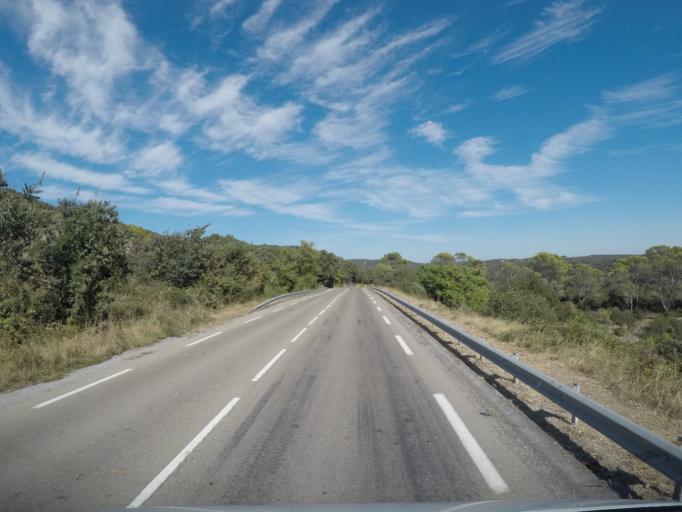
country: FR
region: Languedoc-Roussillon
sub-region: Departement du Gard
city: Sauve
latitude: 43.9621
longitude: 3.9111
